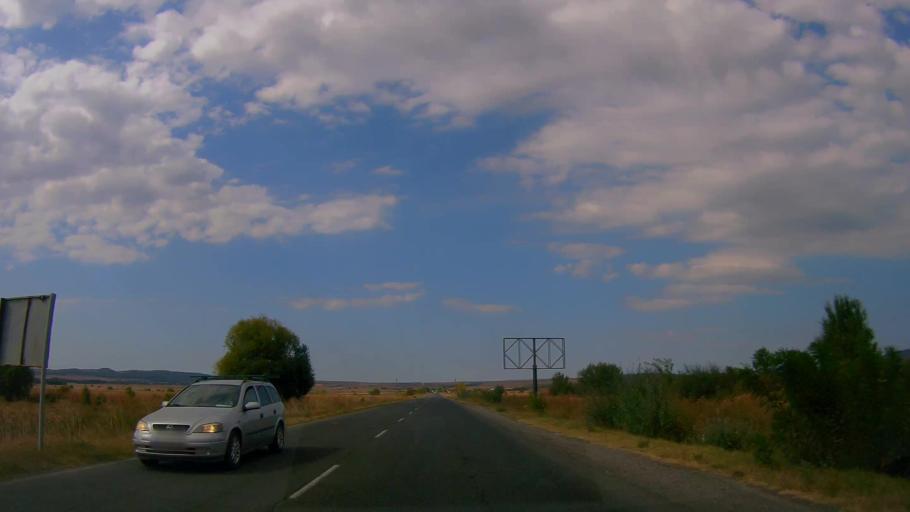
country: BG
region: Burgas
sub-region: Obshtina Aytos
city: Aytos
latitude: 42.7046
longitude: 27.2301
